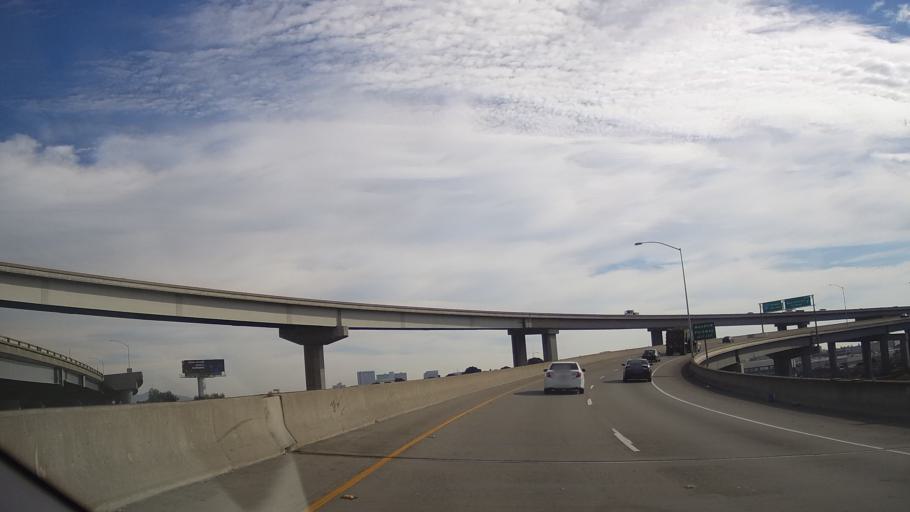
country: US
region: California
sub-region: Alameda County
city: Emeryville
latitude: 37.8269
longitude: -122.2924
